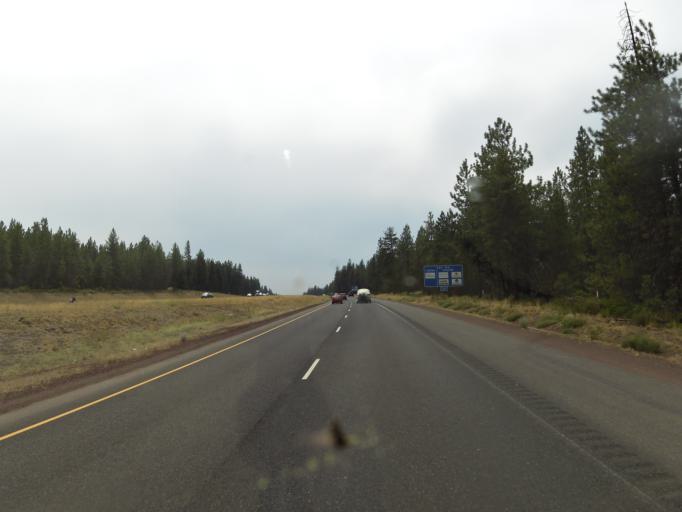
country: US
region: Oregon
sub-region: Deschutes County
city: Sunriver
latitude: 43.8777
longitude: -121.3972
